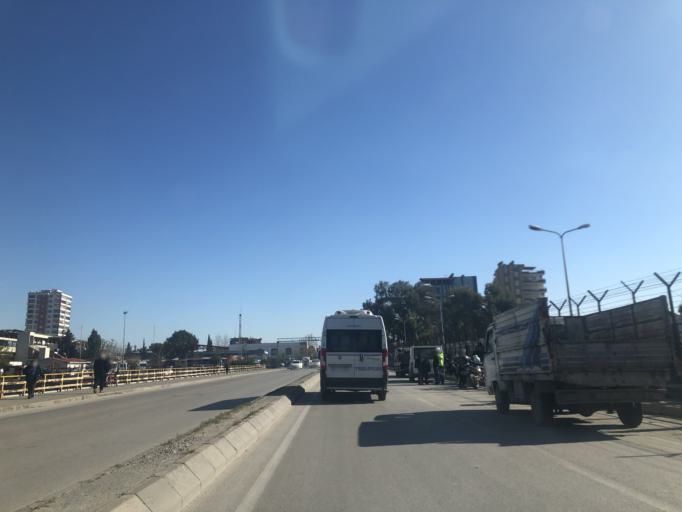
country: TR
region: Adana
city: Adana
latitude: 36.9801
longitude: 35.3350
